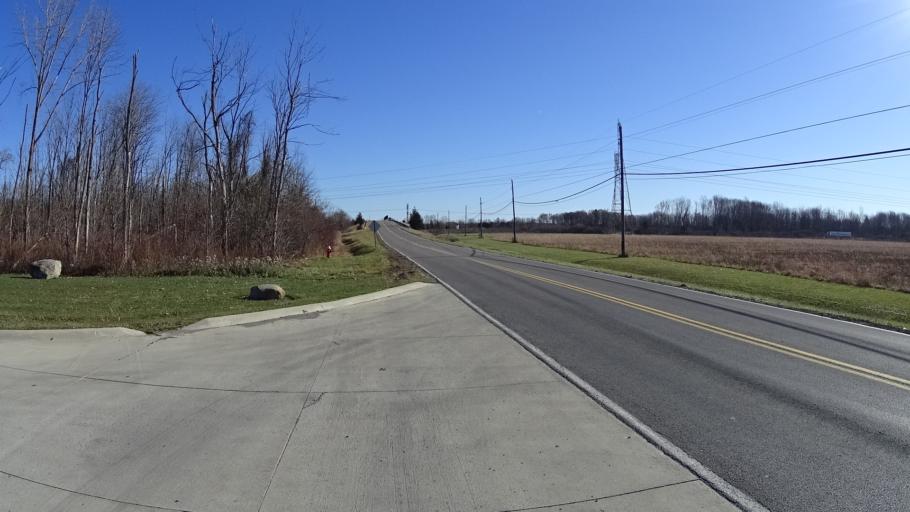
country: US
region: Ohio
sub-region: Lorain County
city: Sheffield
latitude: 41.4495
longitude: -82.0754
